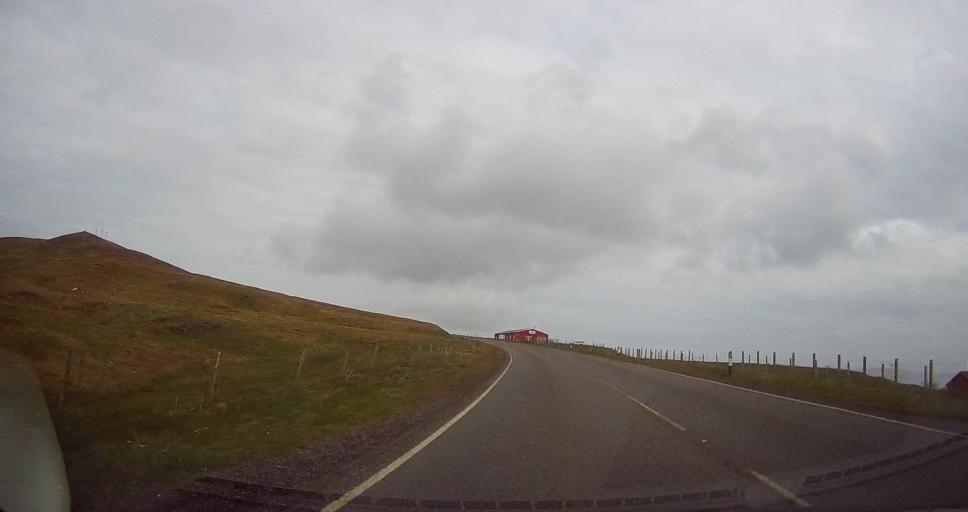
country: GB
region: Scotland
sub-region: Shetland Islands
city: Sandwick
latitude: 60.0602
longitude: -1.2222
